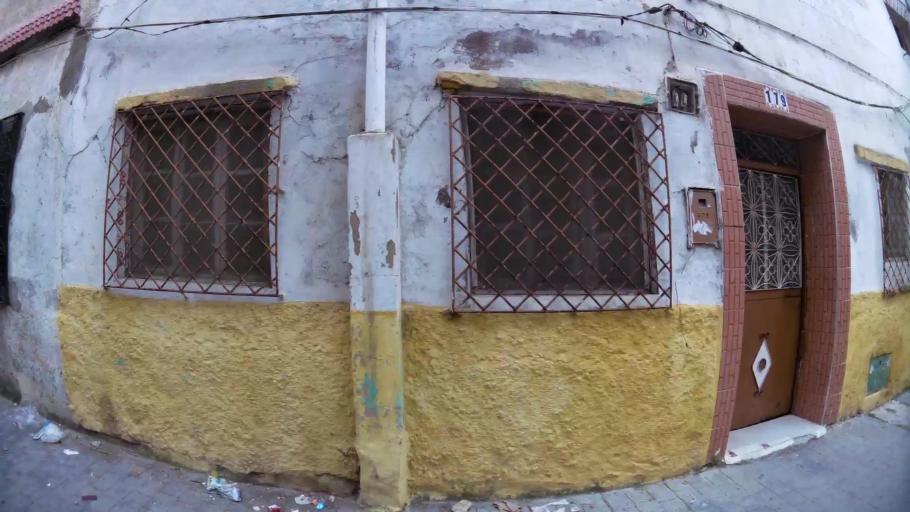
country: MA
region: Tanger-Tetouan
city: Tetouan
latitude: 35.5731
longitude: -5.3858
